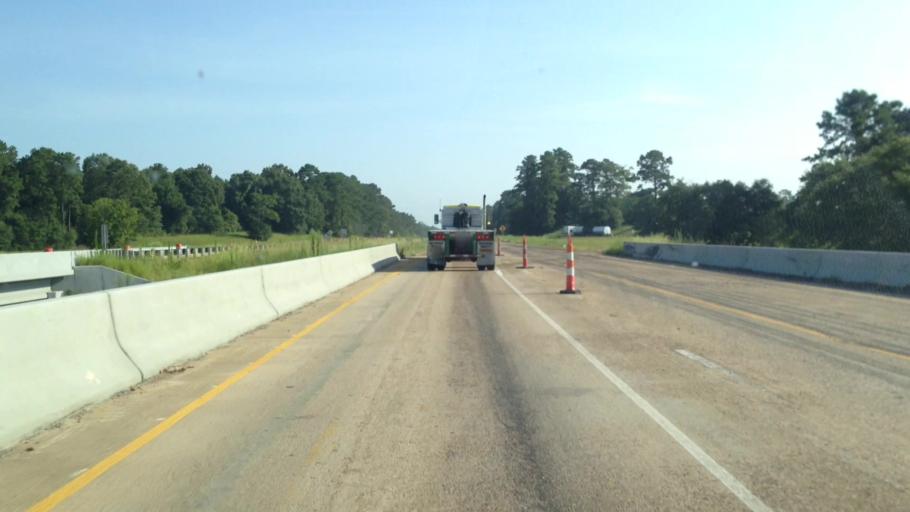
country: US
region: Mississippi
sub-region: Pike County
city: McComb
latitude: 31.2210
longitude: -90.4829
